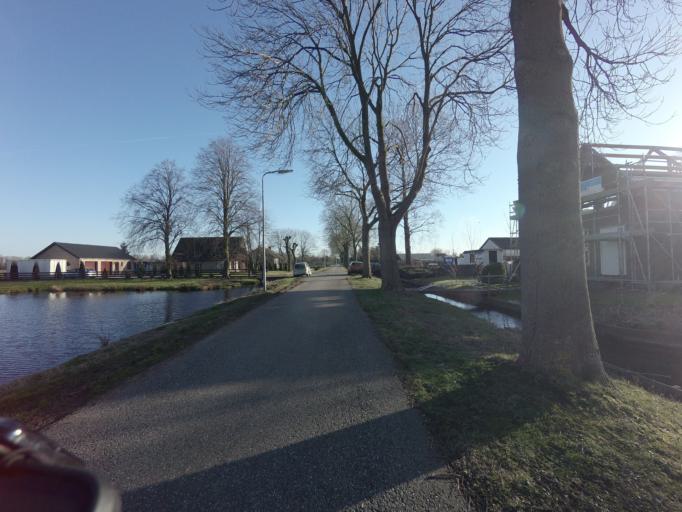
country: NL
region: Utrecht
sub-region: Gemeente De Ronde Venen
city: Mijdrecht
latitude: 52.1710
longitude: 4.8555
